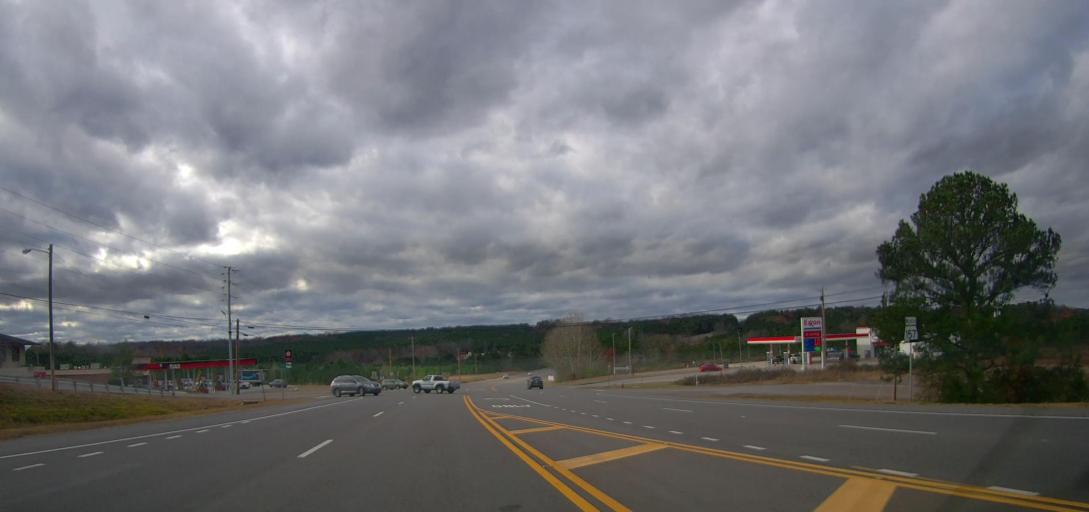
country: US
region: Alabama
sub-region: Cullman County
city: Cullman
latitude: 34.2077
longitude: -86.8807
